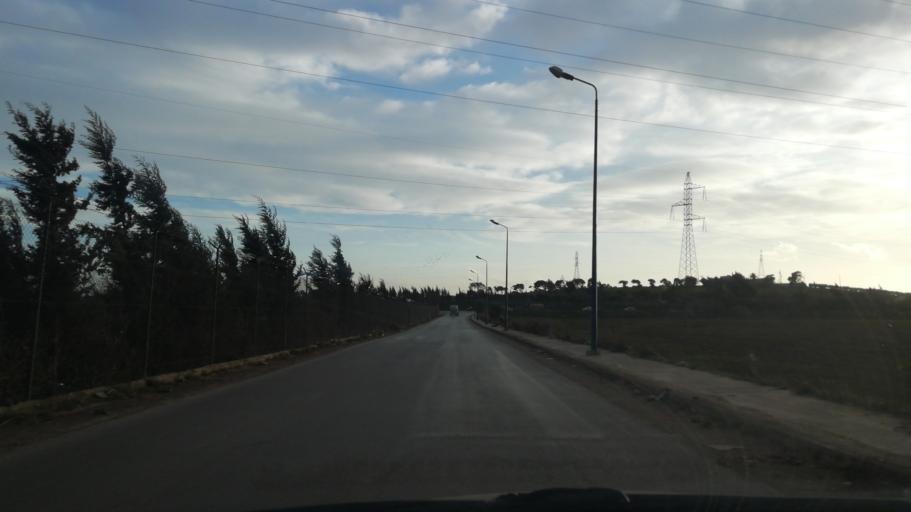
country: DZ
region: Oran
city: Es Senia
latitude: 35.6772
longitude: -0.5908
